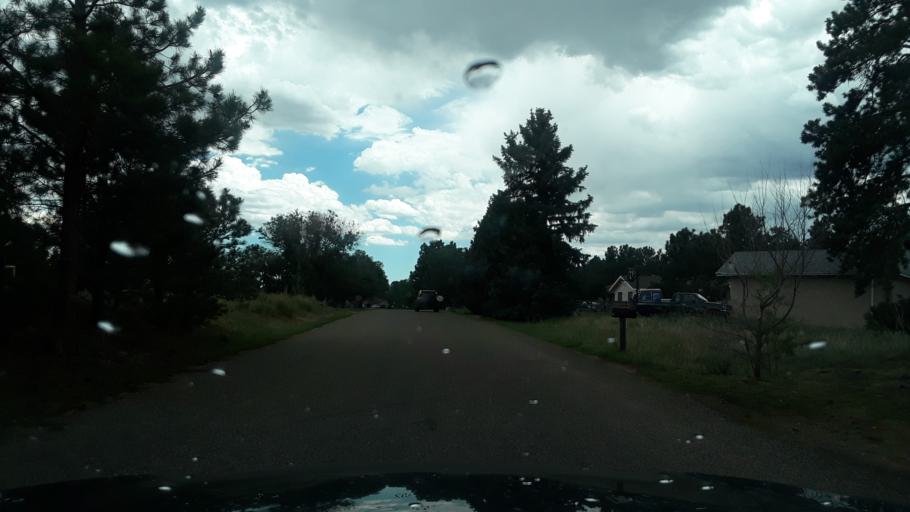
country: US
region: Colorado
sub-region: El Paso County
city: Air Force Academy
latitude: 38.9420
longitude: -104.8184
